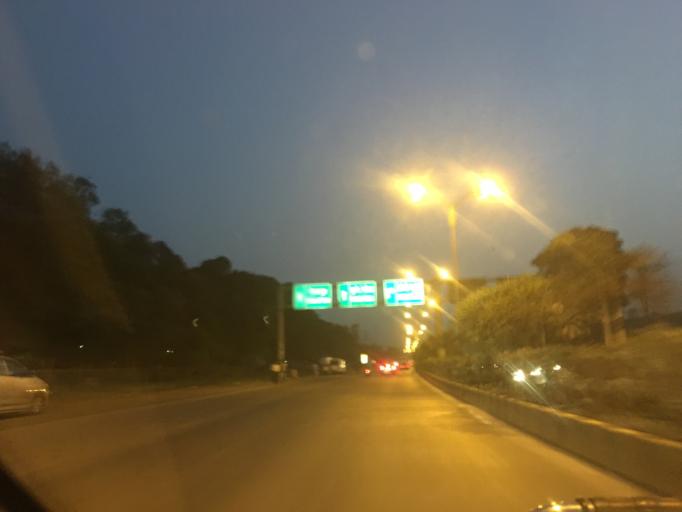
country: IN
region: Maharashtra
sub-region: Thane
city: Airoli
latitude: 19.1520
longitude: 73.0007
